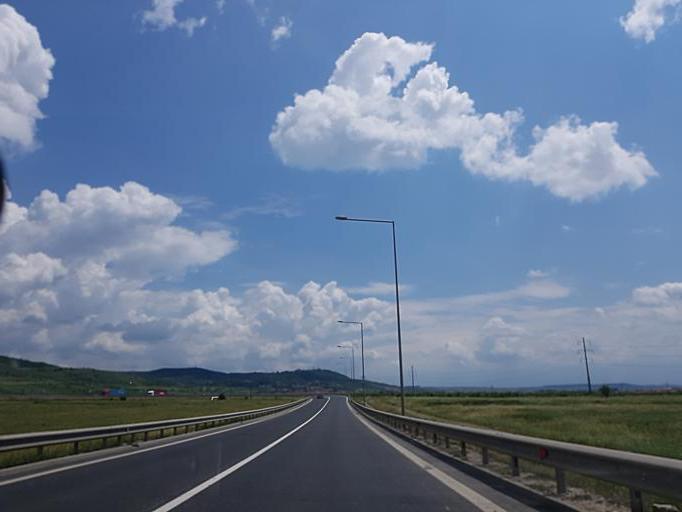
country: RO
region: Sibiu
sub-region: Municipiul Sibiu
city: Sibiu
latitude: 45.8208
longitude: 24.1554
